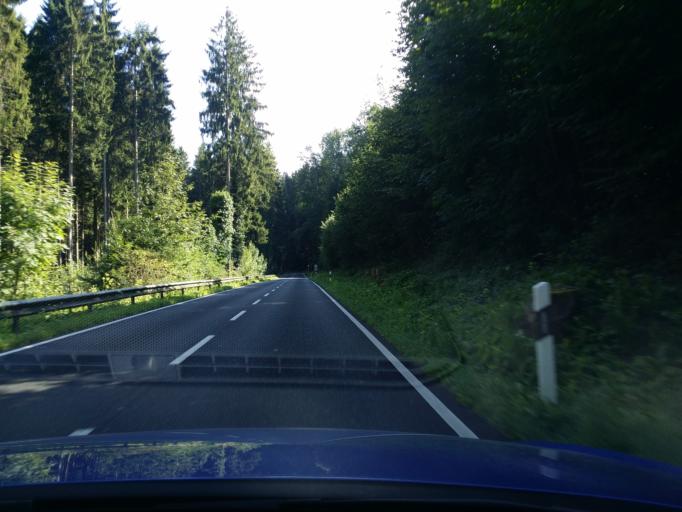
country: LU
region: Luxembourg
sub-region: Canton de Capellen
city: Kopstal
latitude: 49.6940
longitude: 6.0895
